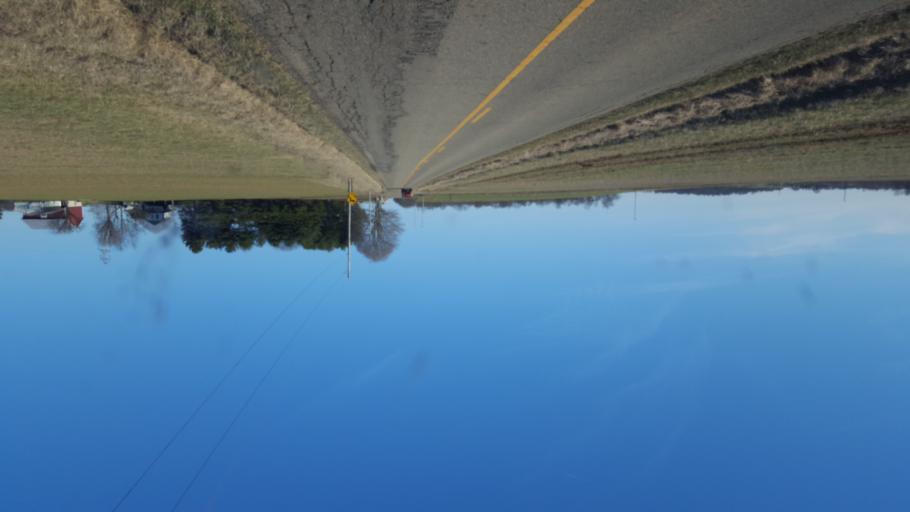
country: US
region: Ohio
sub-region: Knox County
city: Gambier
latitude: 40.4903
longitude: -82.3828
